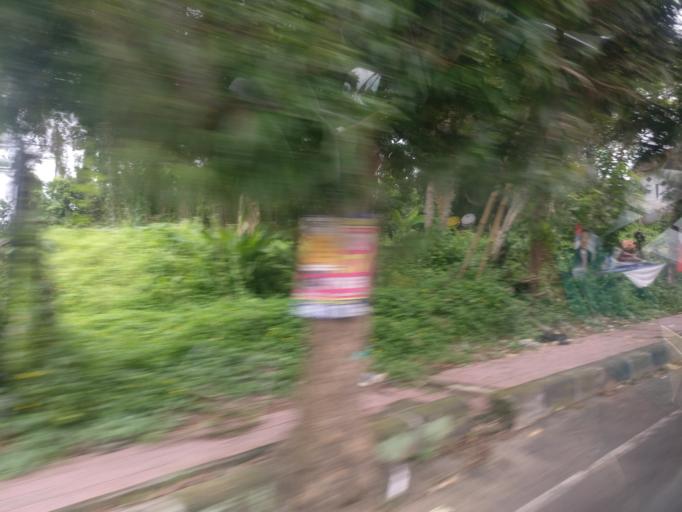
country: ID
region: Bali
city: Banjar Ubud
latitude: -8.4888
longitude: 115.2759
